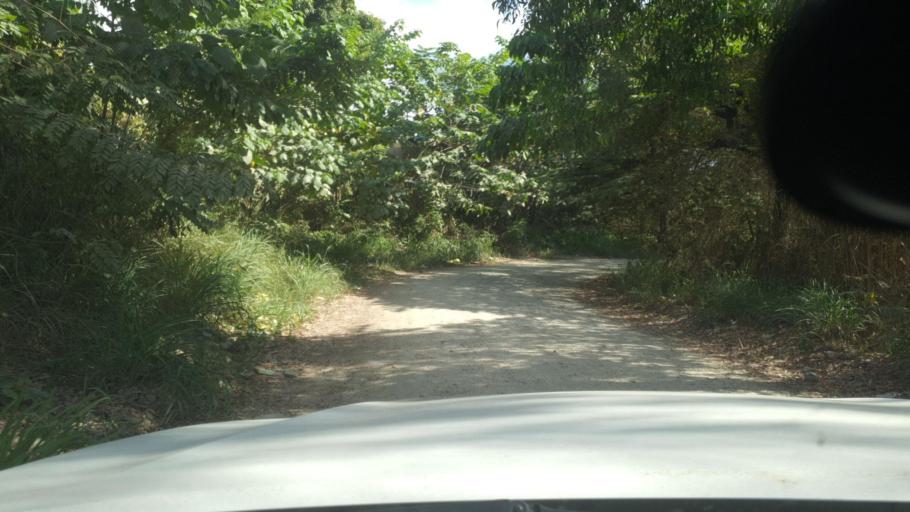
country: SB
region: Guadalcanal
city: Honiara
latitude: -9.4382
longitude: 159.9474
